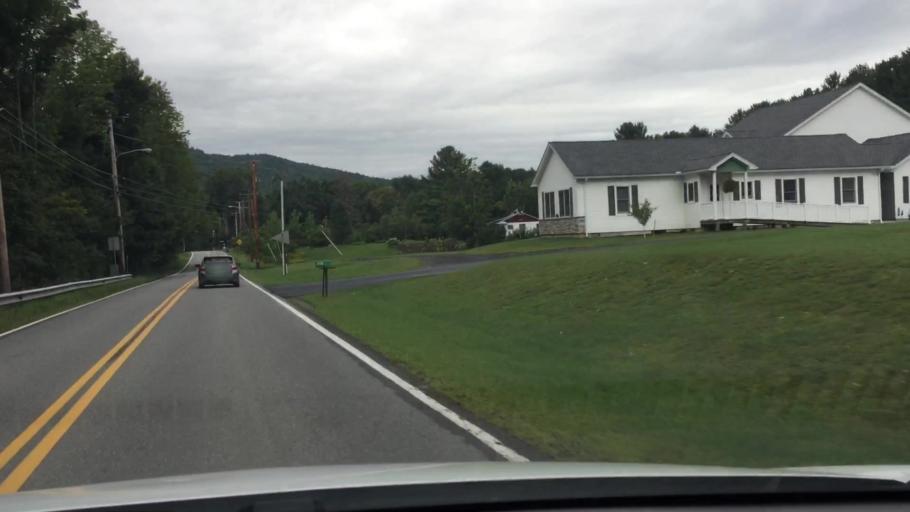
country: US
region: Massachusetts
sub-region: Berkshire County
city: Housatonic
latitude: 42.2586
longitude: -73.3768
